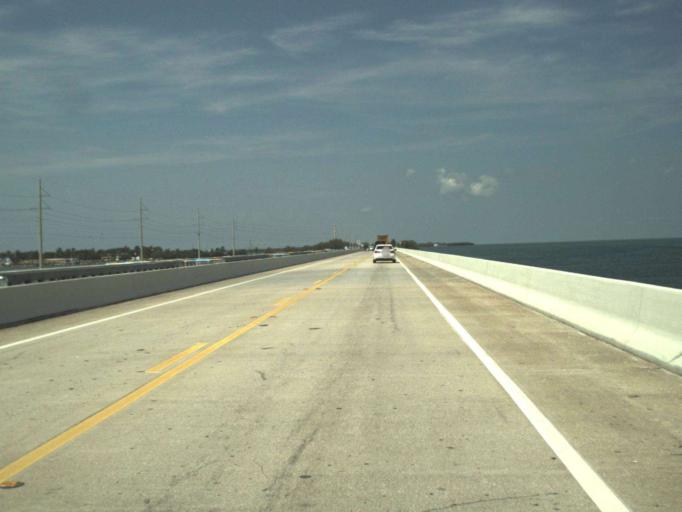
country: US
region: Florida
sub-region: Monroe County
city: Marathon
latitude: 24.7832
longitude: -80.9066
